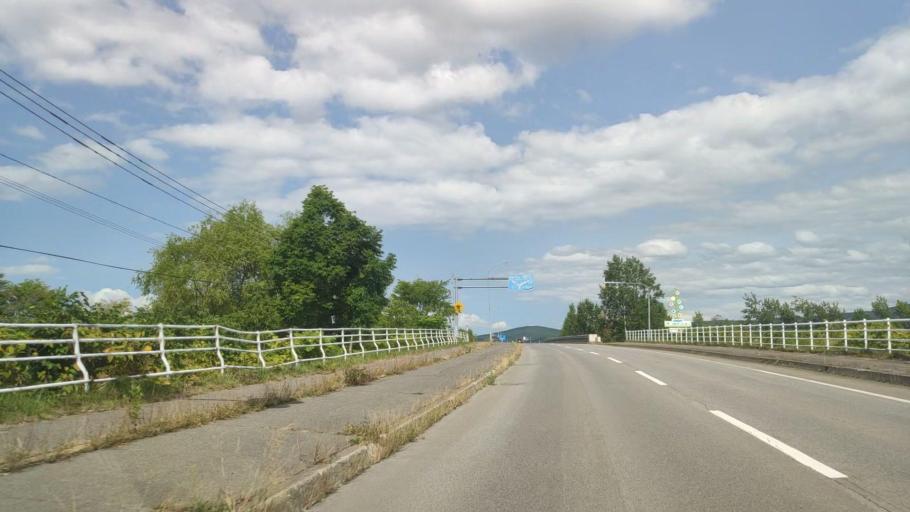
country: JP
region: Hokkaido
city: Nayoro
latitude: 44.1894
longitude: 142.4123
